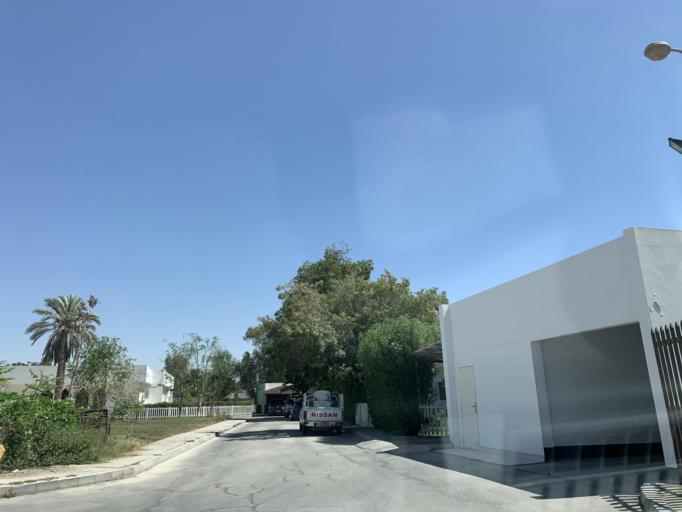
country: BH
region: Manama
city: Jidd Hafs
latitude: 26.2260
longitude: 50.4879
